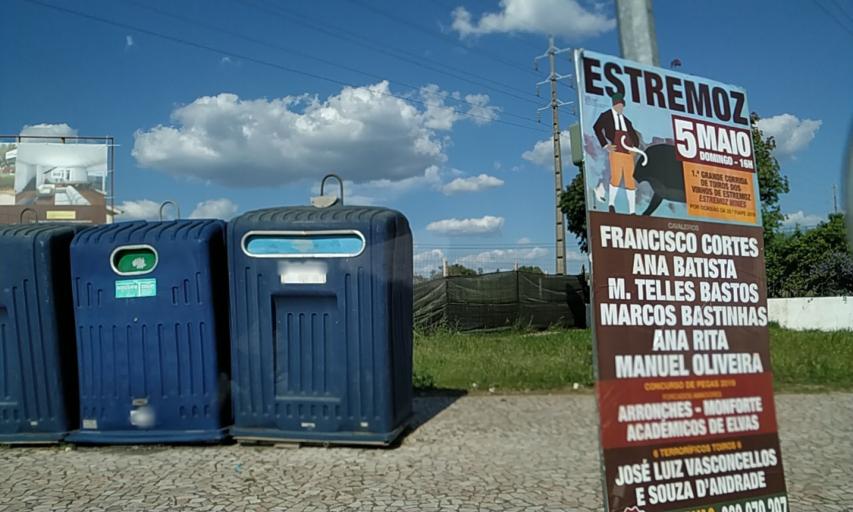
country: PT
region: Evora
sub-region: Estremoz
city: Estremoz
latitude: 38.8506
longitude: -7.5844
